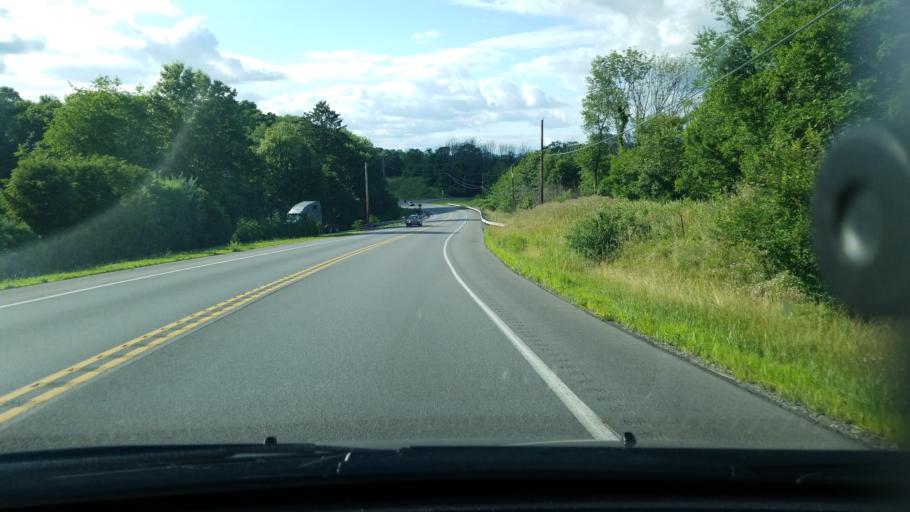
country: US
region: Pennsylvania
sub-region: Northumberland County
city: Elysburg
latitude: 40.8875
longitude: -76.5569
